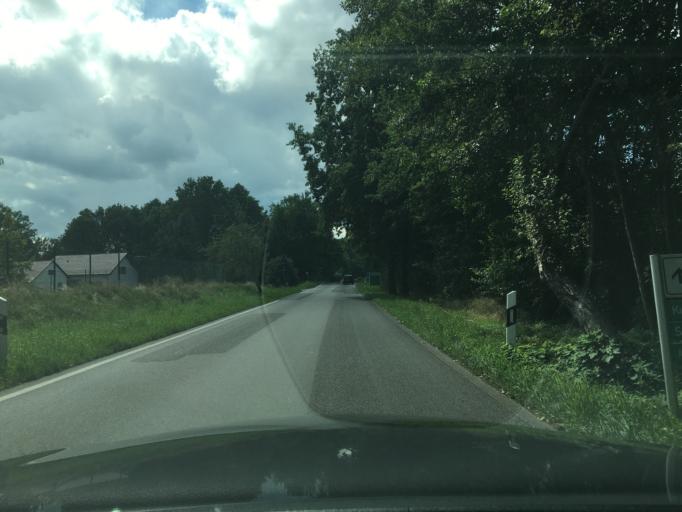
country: DE
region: Brandenburg
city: Burg
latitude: 51.8446
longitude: 14.1087
